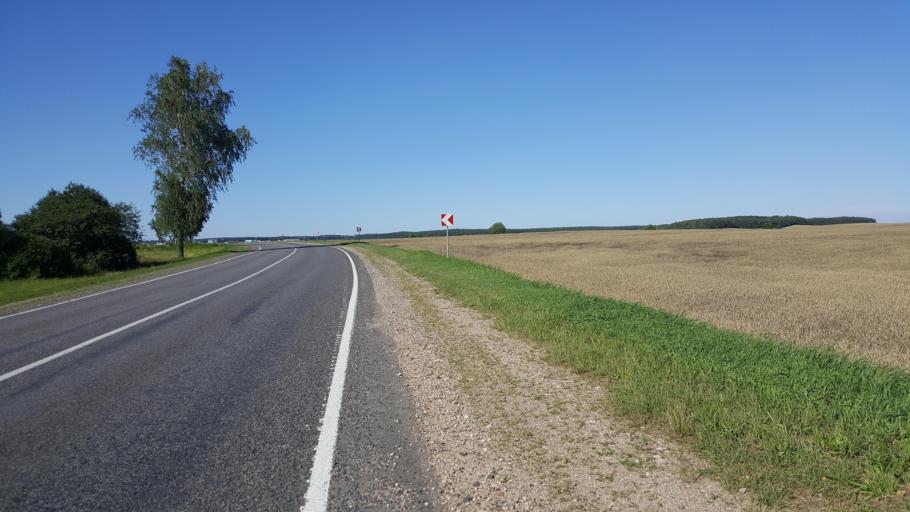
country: BY
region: Brest
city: Charnawchytsy
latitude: 52.3007
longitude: 23.7810
